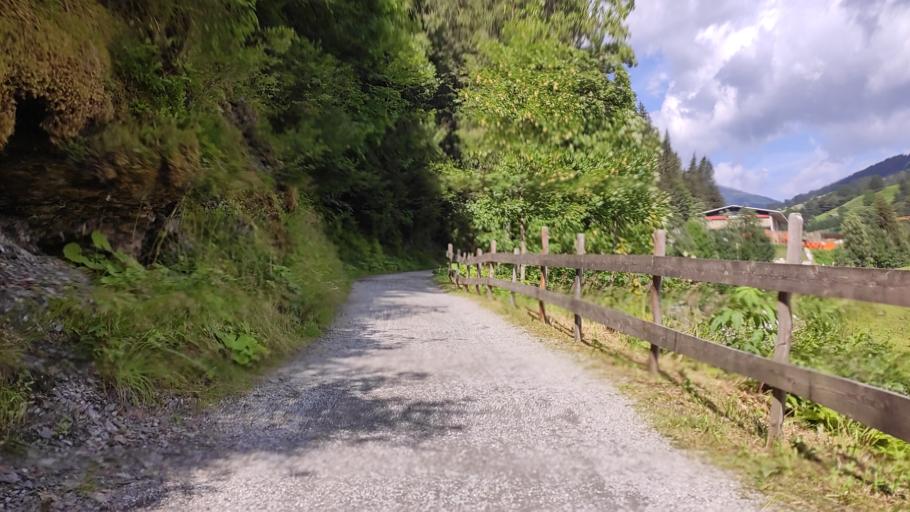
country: AT
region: Salzburg
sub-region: Politischer Bezirk Zell am See
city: Saalbach
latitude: 47.3802
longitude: 12.6693
